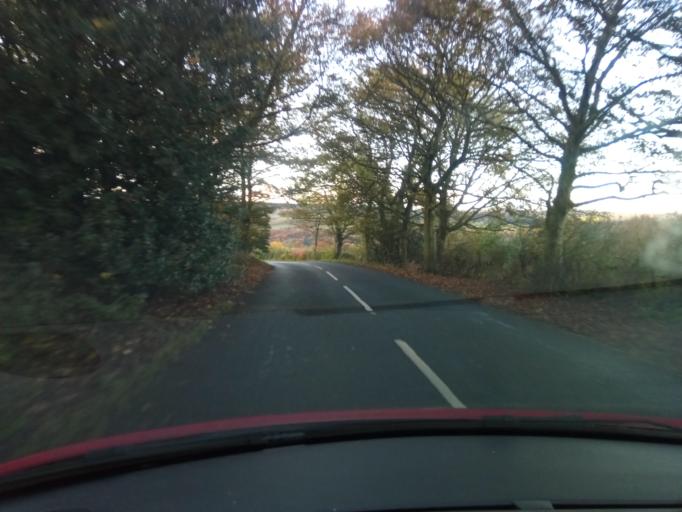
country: GB
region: England
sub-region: County Durham
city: Hamsterley
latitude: 54.6772
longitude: -1.8273
